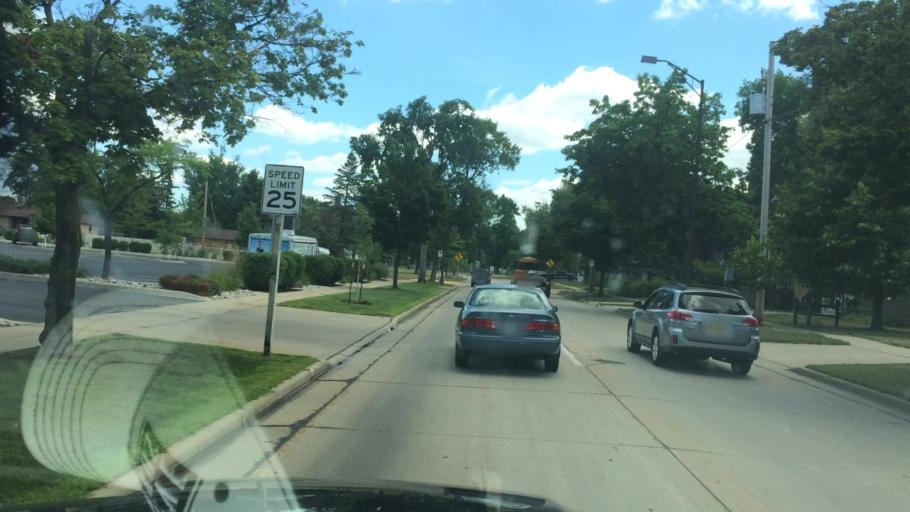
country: US
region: Wisconsin
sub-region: Portage County
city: Stevens Point
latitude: 44.5224
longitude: -89.5623
